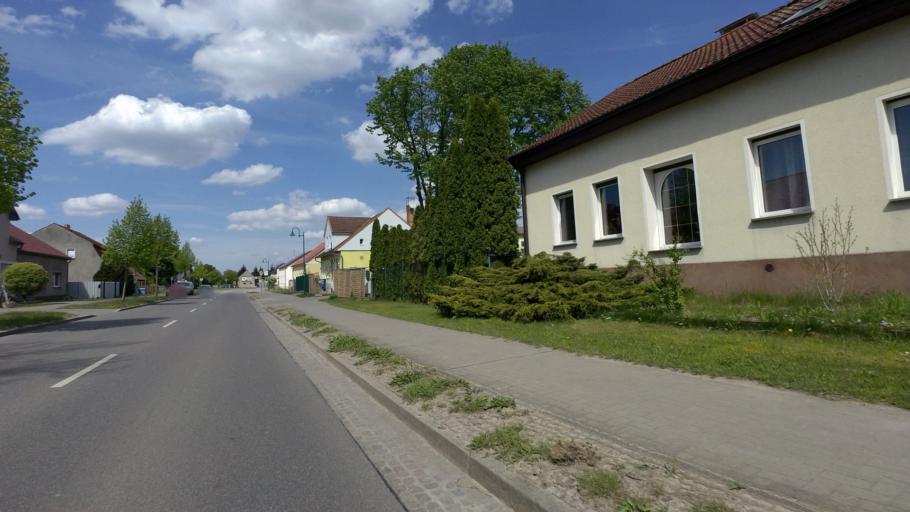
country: DE
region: Brandenburg
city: Wandlitz
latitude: 52.7957
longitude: 13.4796
